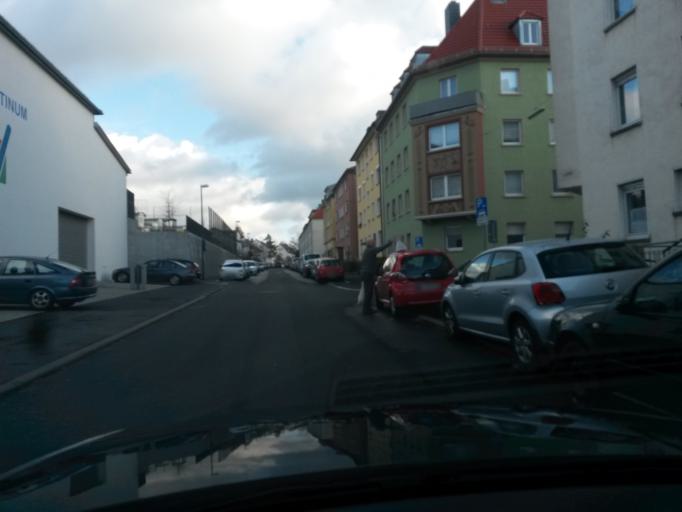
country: DE
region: Bavaria
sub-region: Regierungsbezirk Unterfranken
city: Wuerzburg
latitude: 49.8040
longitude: 9.9468
